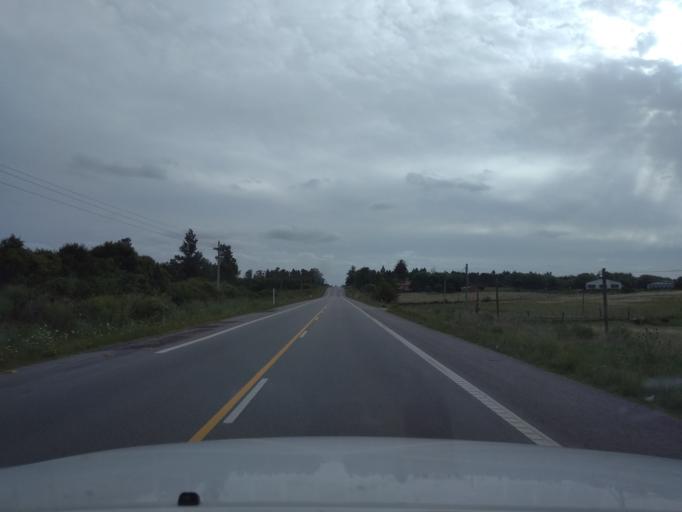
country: UY
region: Canelones
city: Joaquin Suarez
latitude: -34.6881
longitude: -56.0252
